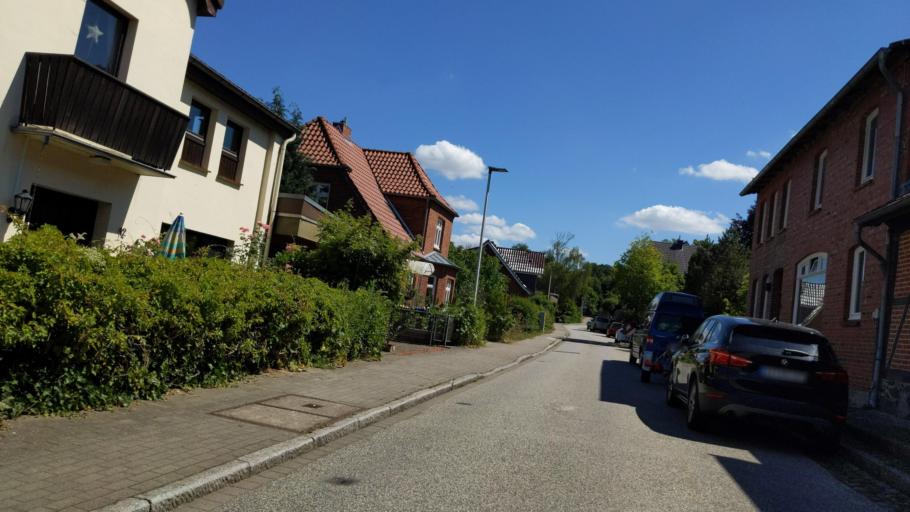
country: DE
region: Schleswig-Holstein
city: Romnitz
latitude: 53.7018
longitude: 10.7522
